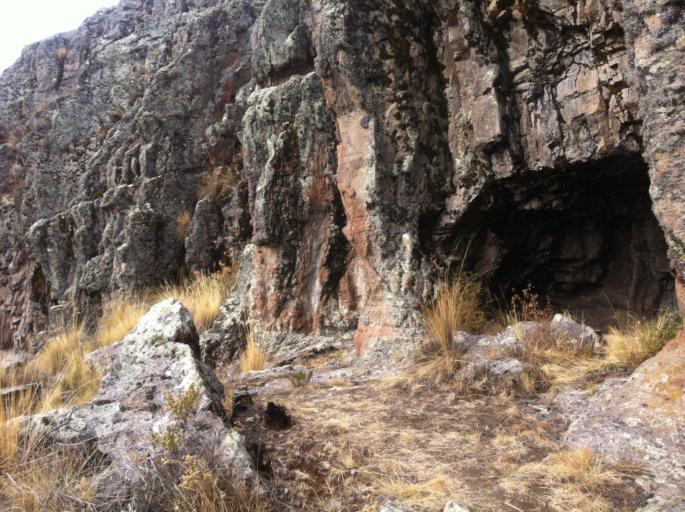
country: PE
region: Puno
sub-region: Yunguyo
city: Yunguyo
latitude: -16.1942
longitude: -69.0806
